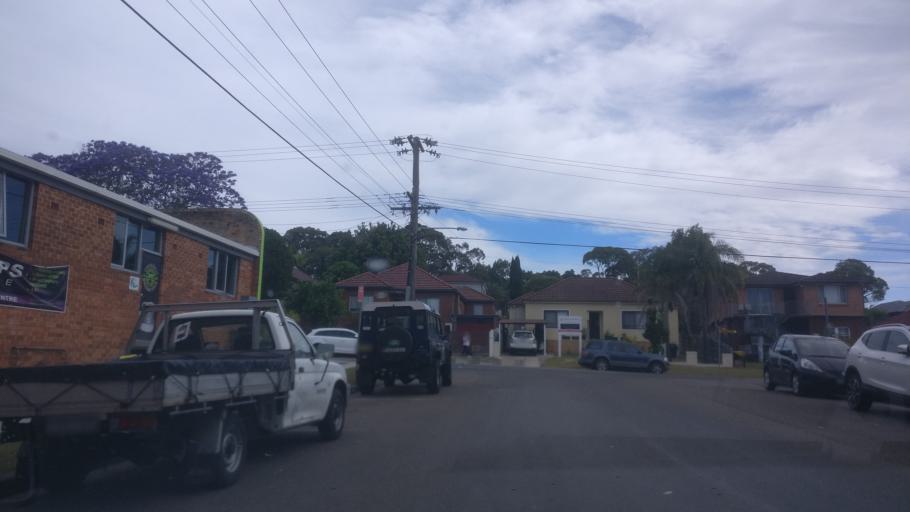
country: AU
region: New South Wales
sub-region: Warringah
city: Brookvale
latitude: -33.7677
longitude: 151.2767
